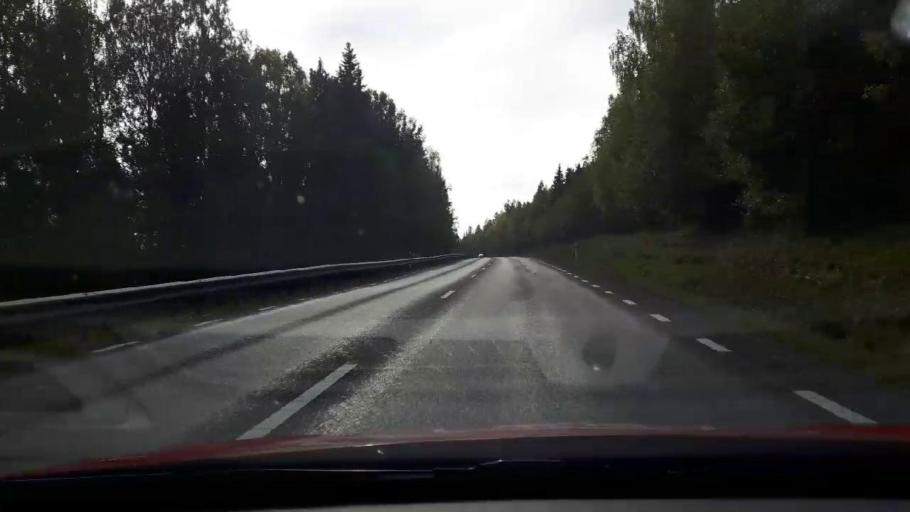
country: SE
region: Gaevleborg
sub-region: Ljusdals Kommun
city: Jaervsoe
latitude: 61.7417
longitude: 16.1588
